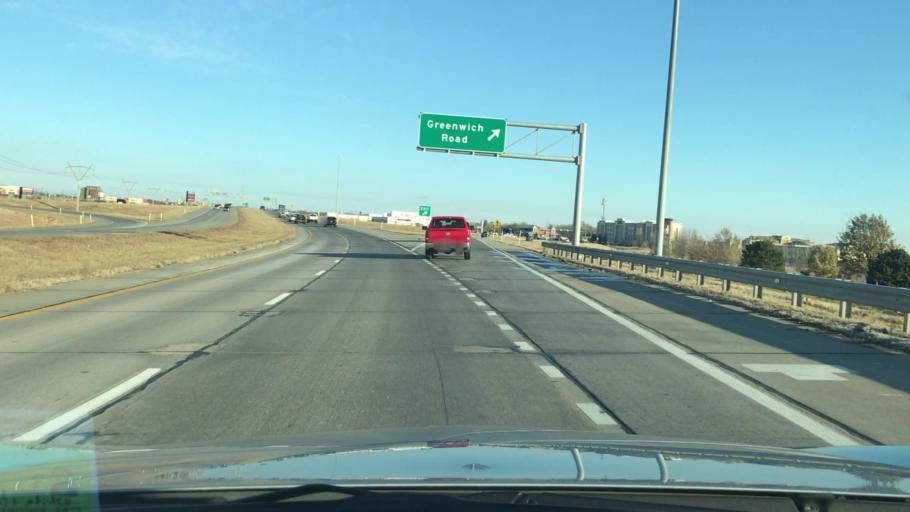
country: US
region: Kansas
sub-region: Sedgwick County
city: Bellaire
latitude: 37.7299
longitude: -97.2142
